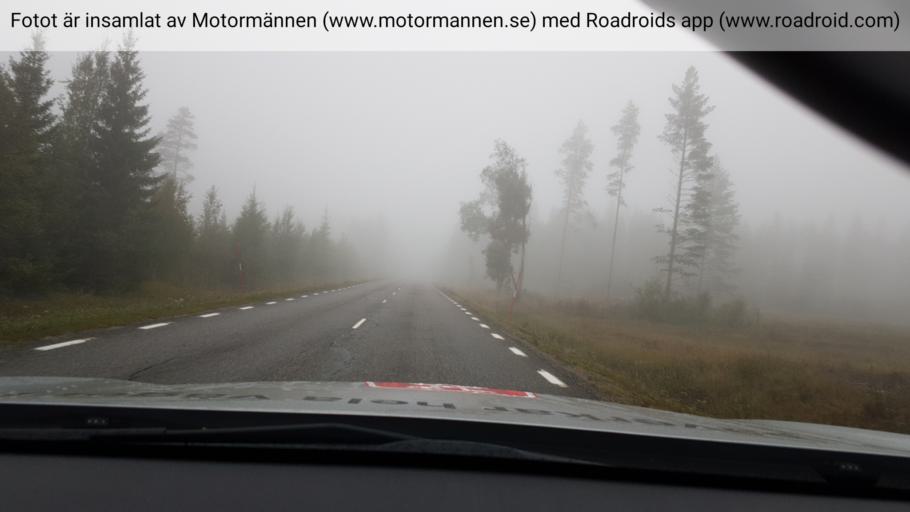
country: SE
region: Vaesterbotten
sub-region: Umea Kommun
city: Ersmark
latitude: 64.1128
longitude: 20.1700
